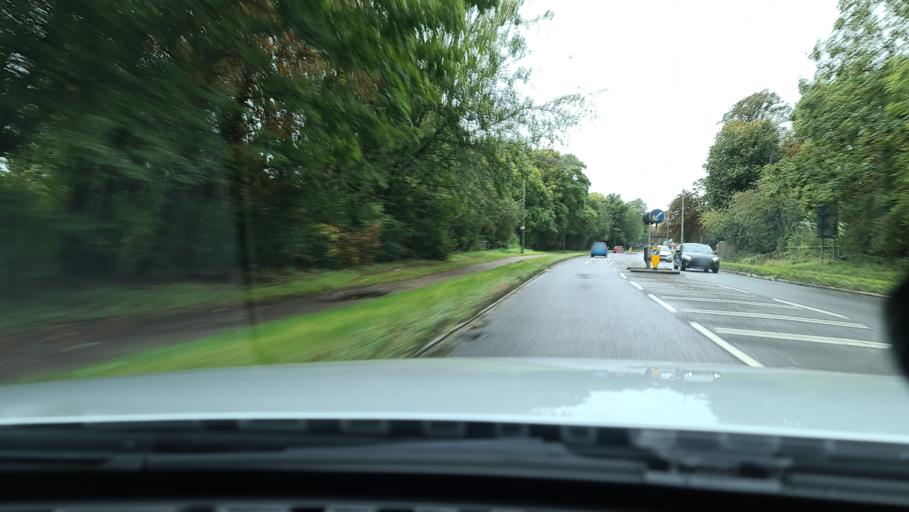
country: GB
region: England
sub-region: Milton Keynes
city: Stony Stratford
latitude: 52.0604
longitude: -0.8361
